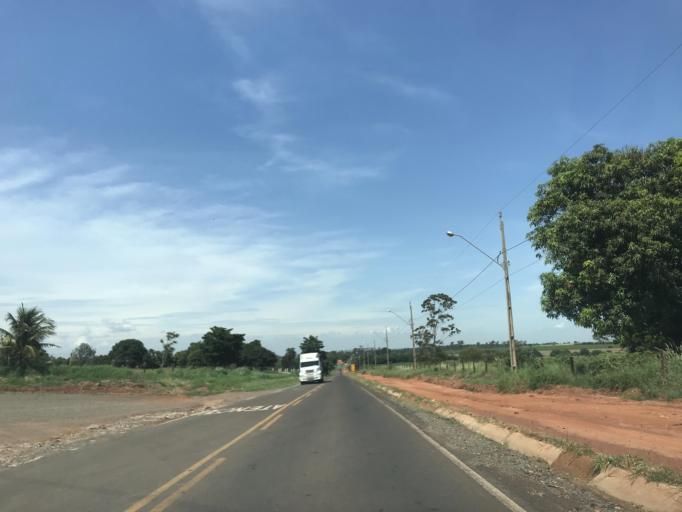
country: BR
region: Parana
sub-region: Paranavai
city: Nova Aurora
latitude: -22.9471
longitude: -52.6978
